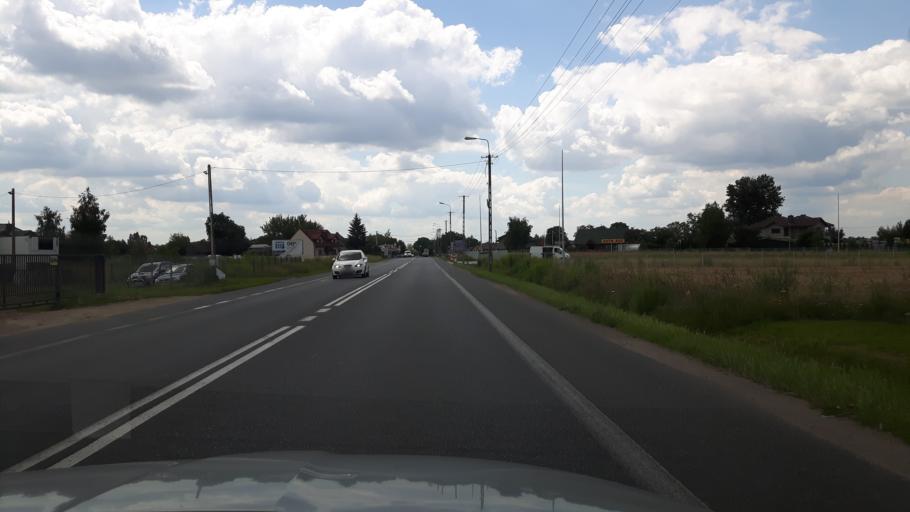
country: PL
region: Masovian Voivodeship
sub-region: Powiat wyszkowski
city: Wyszkow
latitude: 52.6141
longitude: 21.4807
